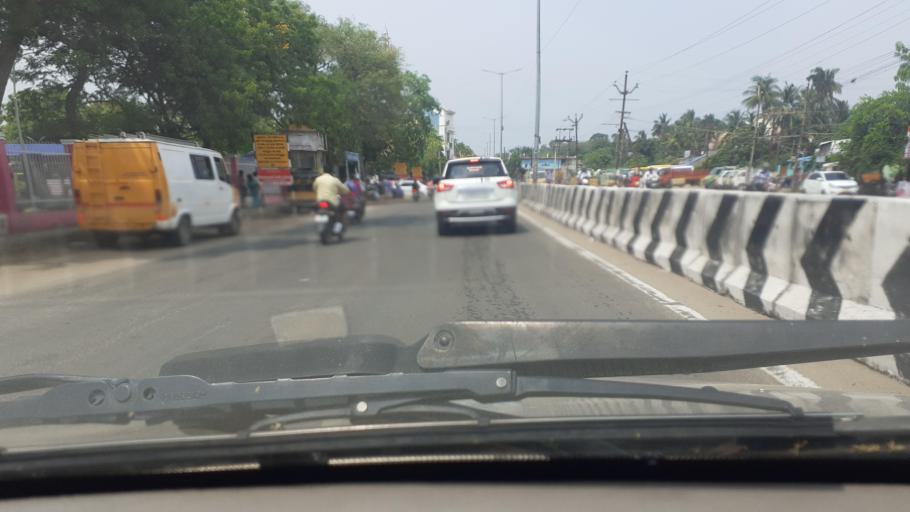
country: IN
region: Tamil Nadu
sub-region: Thoothukkudi
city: Korampallam
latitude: 8.7984
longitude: 78.1316
